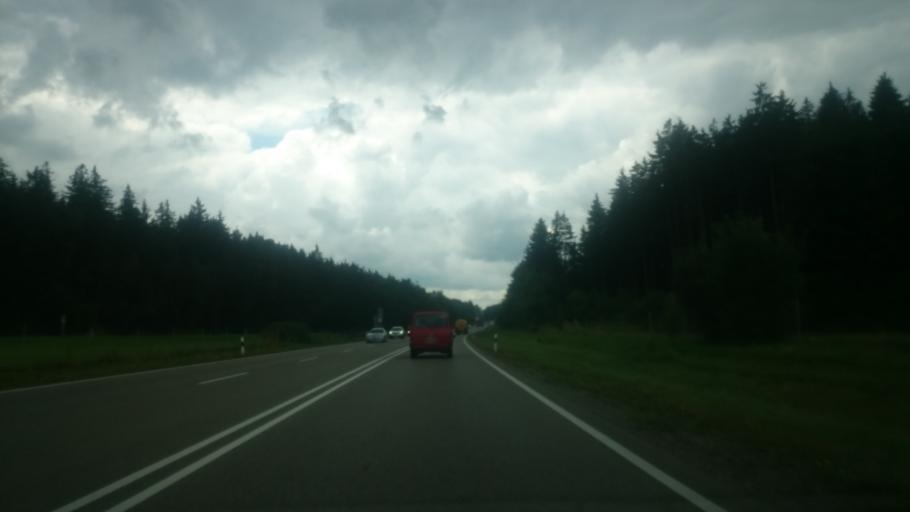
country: DE
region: Bavaria
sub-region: Swabia
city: Mauerstetten
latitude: 47.9087
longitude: 10.6561
